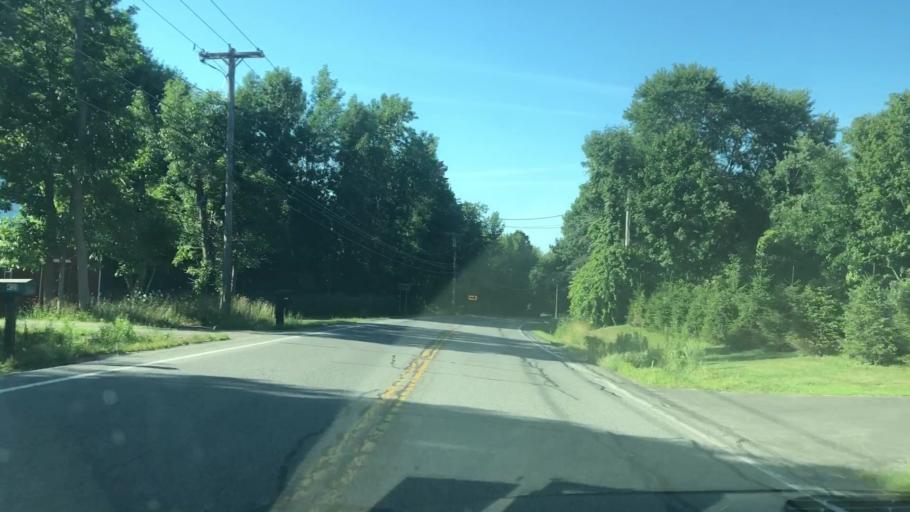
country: US
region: New York
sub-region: Wayne County
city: Ontario
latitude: 43.1526
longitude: -77.2926
